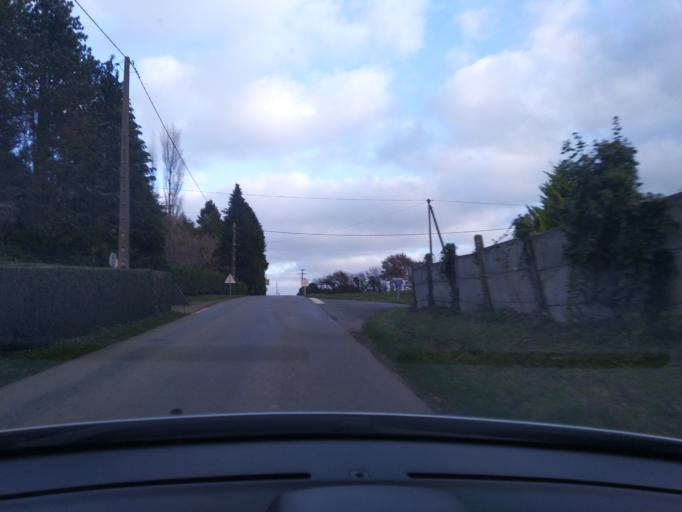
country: FR
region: Brittany
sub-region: Departement du Finistere
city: Plouigneau
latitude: 48.5660
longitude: -3.6542
